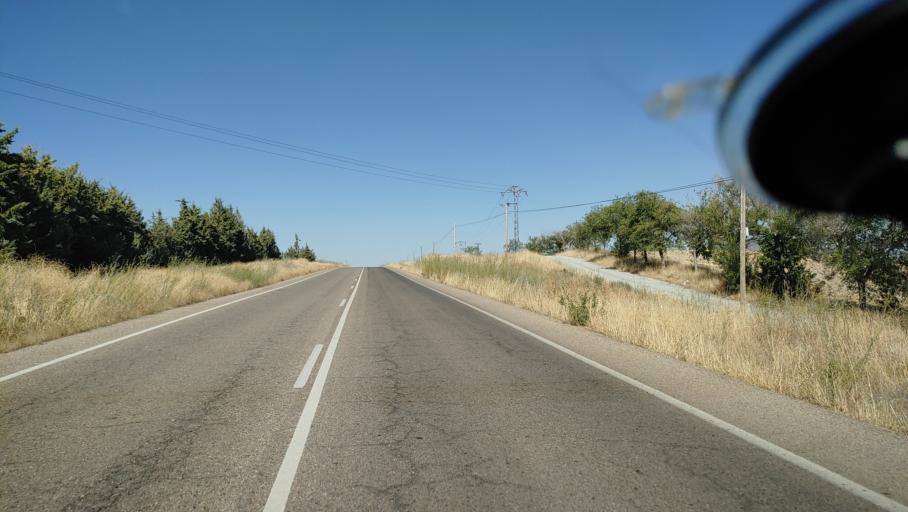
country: ES
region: Castille-La Mancha
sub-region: Province of Toledo
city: Pulgar
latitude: 39.7039
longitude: -4.1420
